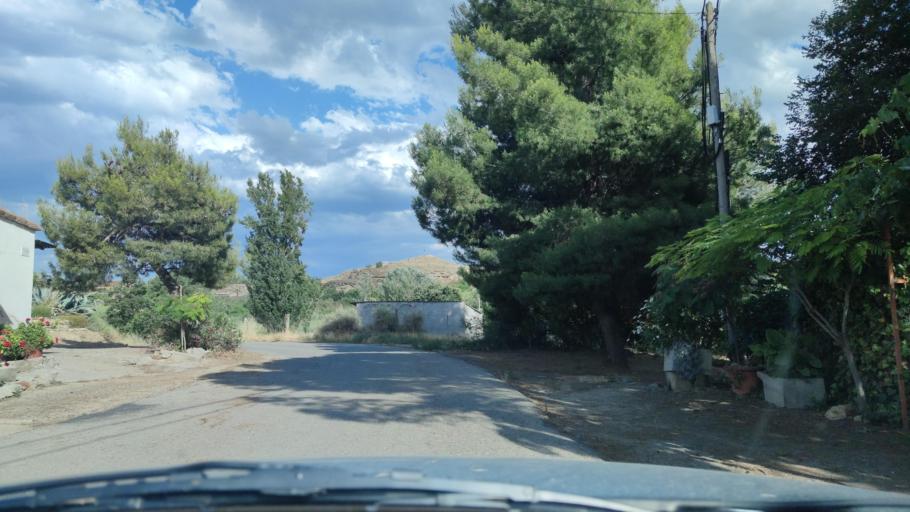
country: ES
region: Catalonia
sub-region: Provincia de Lleida
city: Alpicat
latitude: 41.6315
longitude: 0.5571
